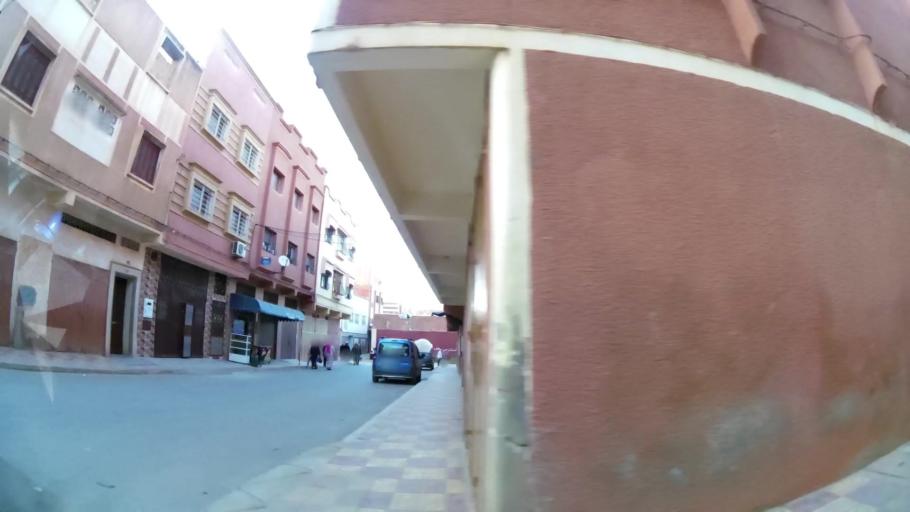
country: MA
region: Oriental
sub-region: Berkane-Taourirt
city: Berkane
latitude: 34.9192
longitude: -2.3192
